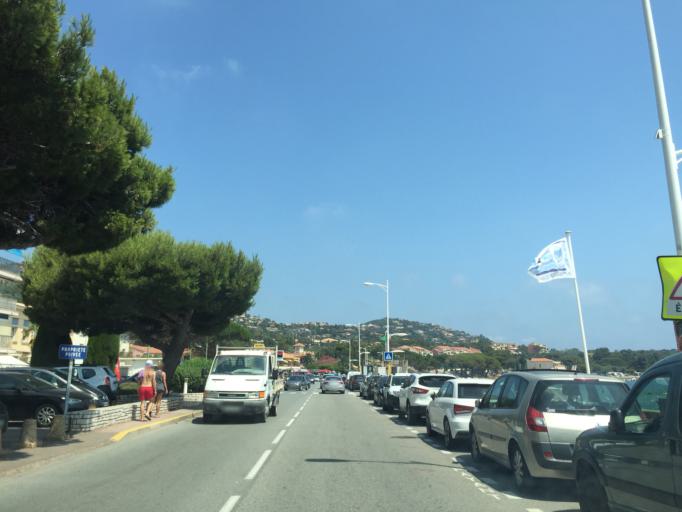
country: FR
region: Provence-Alpes-Cote d'Azur
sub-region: Departement du Var
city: Saint-Raphael
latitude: 43.4343
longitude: 6.8625
